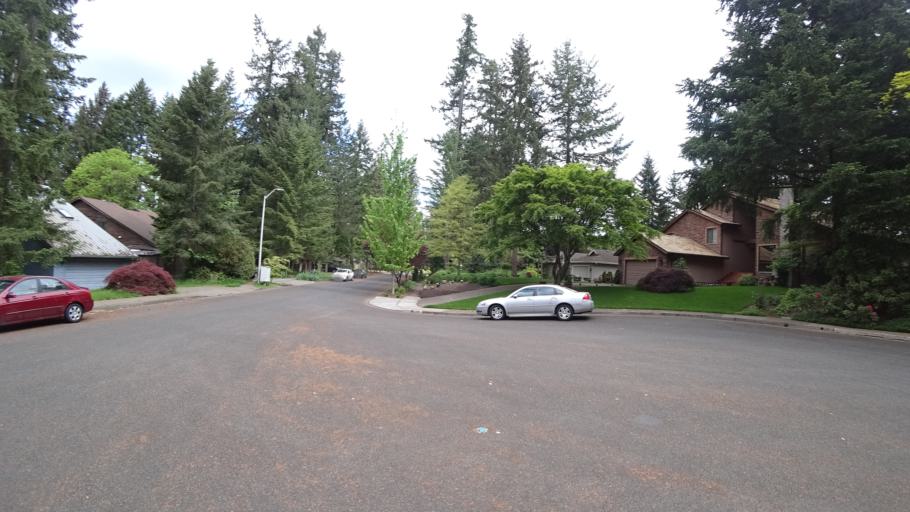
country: US
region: Oregon
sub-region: Washington County
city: Beaverton
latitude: 45.4624
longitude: -122.8324
